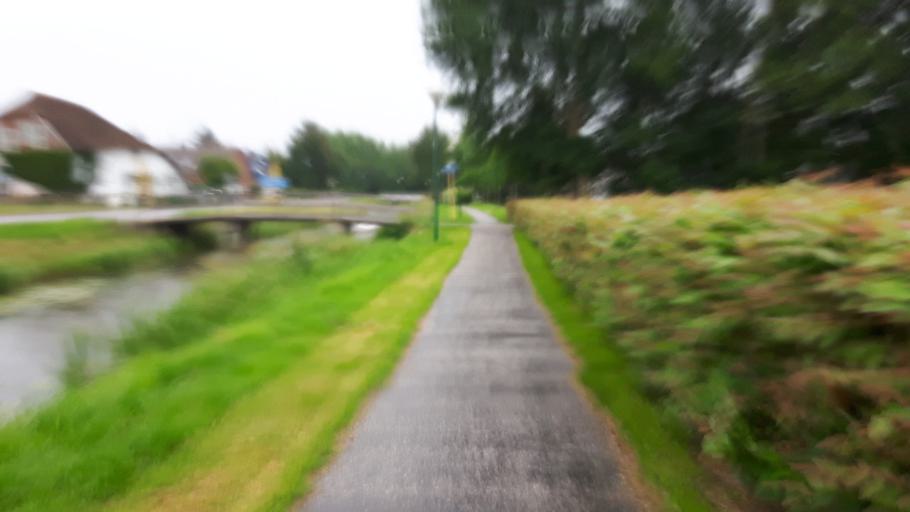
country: NL
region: Utrecht
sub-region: Gemeente IJsselstein
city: IJsselstein
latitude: 51.9929
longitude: 5.0484
